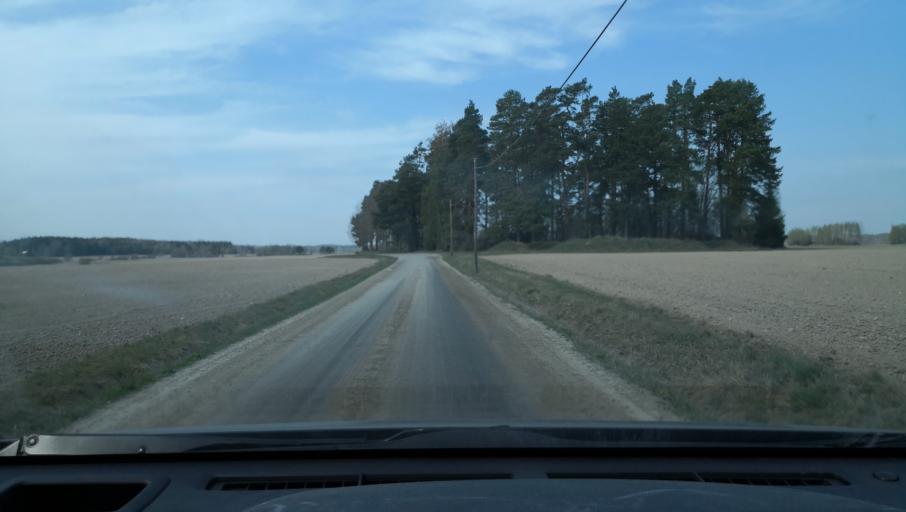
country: SE
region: Vaestmanland
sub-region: Vasteras
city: Skultuna
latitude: 59.7867
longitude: 16.4566
